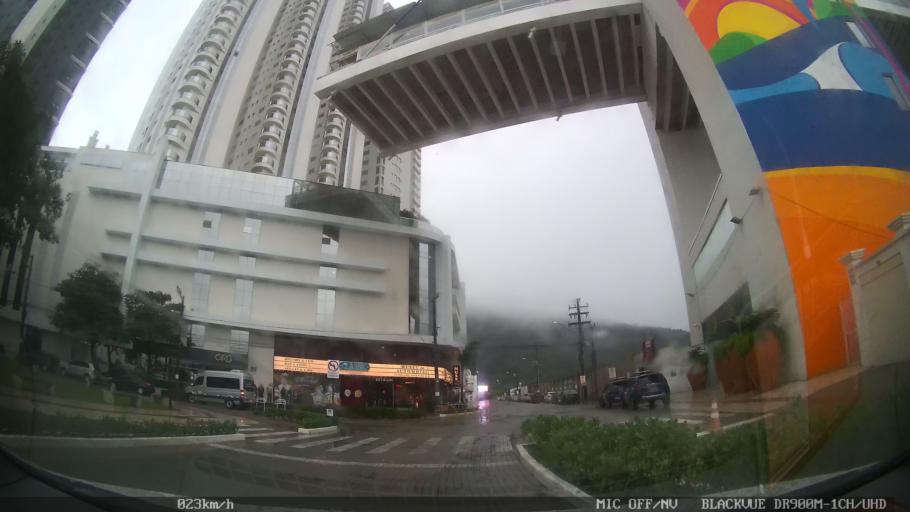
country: BR
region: Santa Catarina
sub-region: Balneario Camboriu
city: Balneario Camboriu
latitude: -27.0067
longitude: -48.6049
